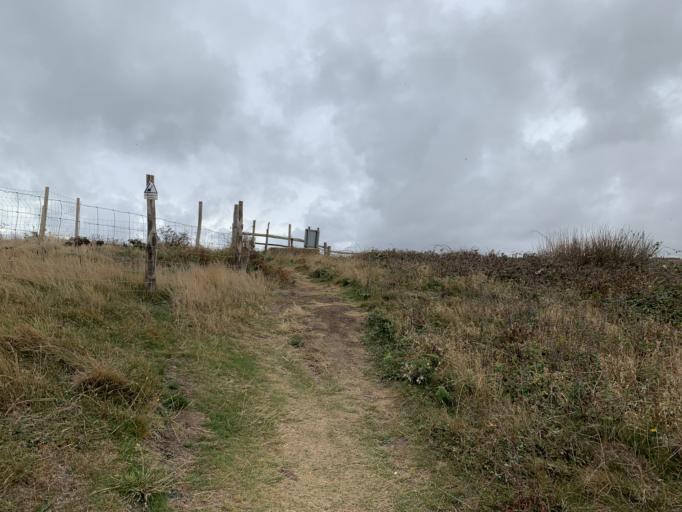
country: GB
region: England
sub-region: East Sussex
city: Newhaven
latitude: 50.7817
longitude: 0.0440
